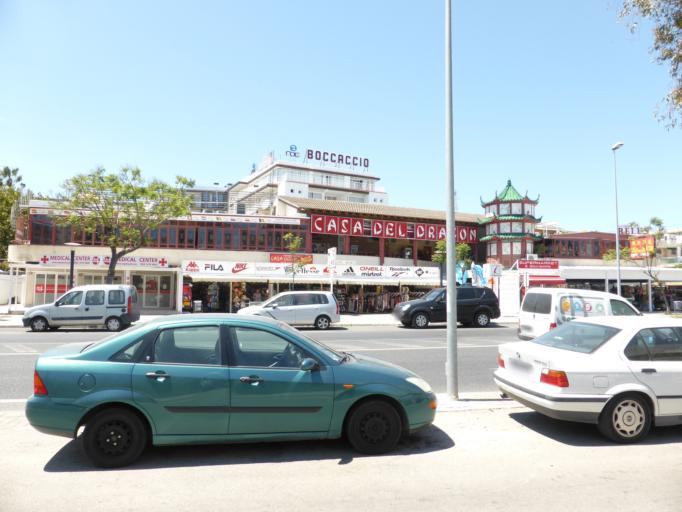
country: ES
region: Balearic Islands
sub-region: Illes Balears
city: Port d'Alcudia
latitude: 39.8310
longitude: 3.1169
